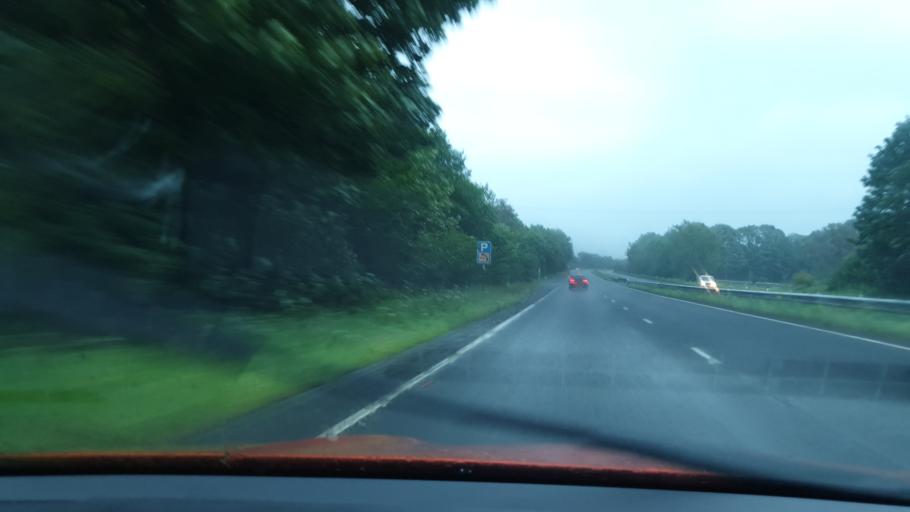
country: GB
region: England
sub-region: Cumbria
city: Grange-over-Sands
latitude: 54.2213
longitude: -2.8867
